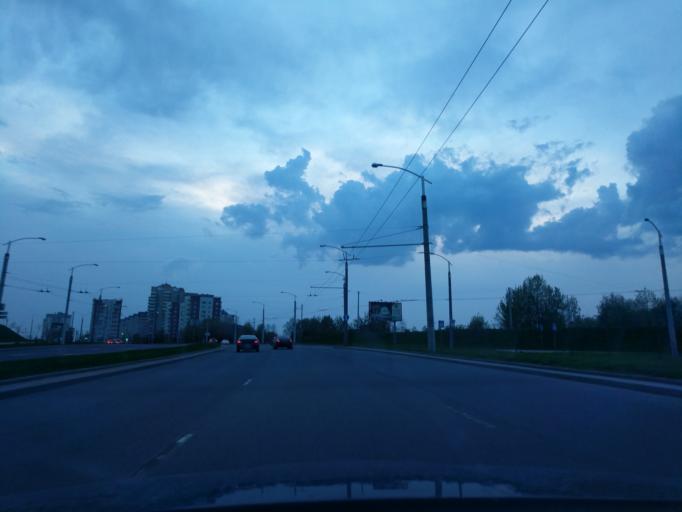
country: BY
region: Minsk
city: Novoye Medvezhino
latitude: 53.8720
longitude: 27.4913
